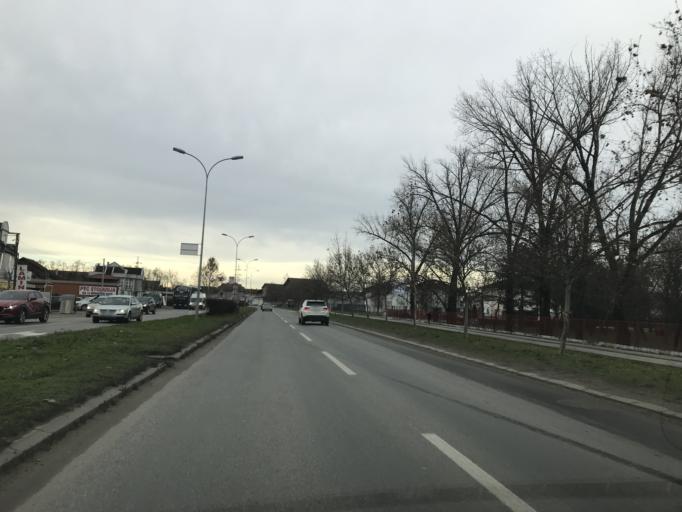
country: RS
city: Veternik
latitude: 45.2448
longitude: 19.7755
